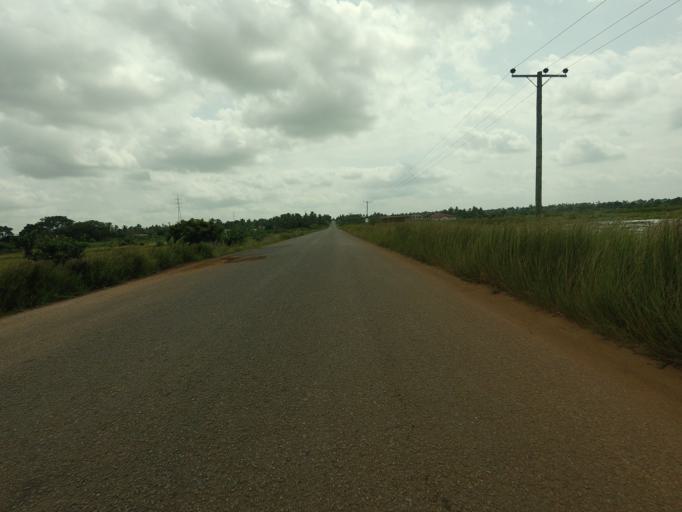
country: TG
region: Maritime
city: Lome
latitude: 6.1705
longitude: 1.0805
